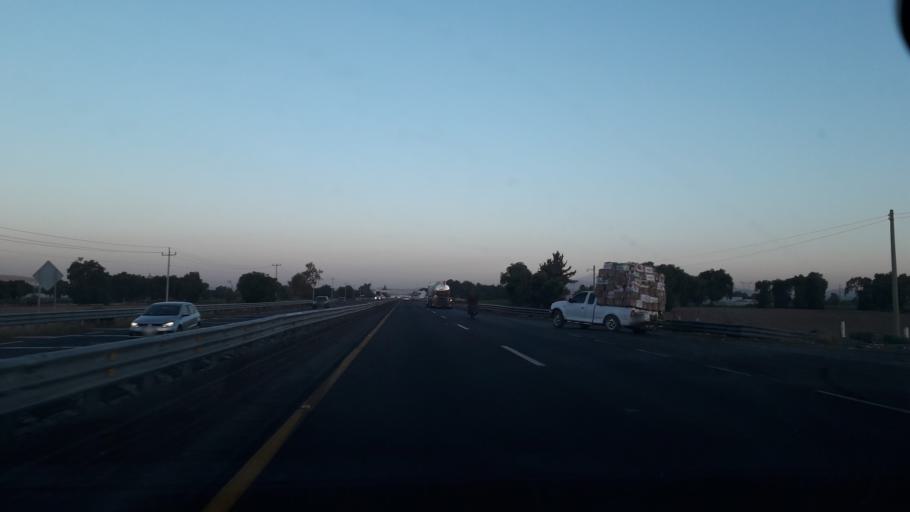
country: MX
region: Puebla
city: Palmarito Tochapan
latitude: 18.9155
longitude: -97.6448
